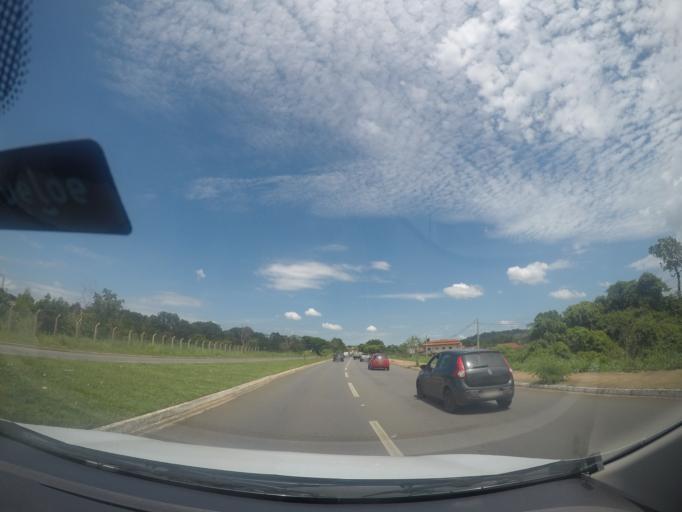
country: BR
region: Goias
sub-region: Goiania
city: Goiania
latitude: -16.6830
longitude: -49.3351
